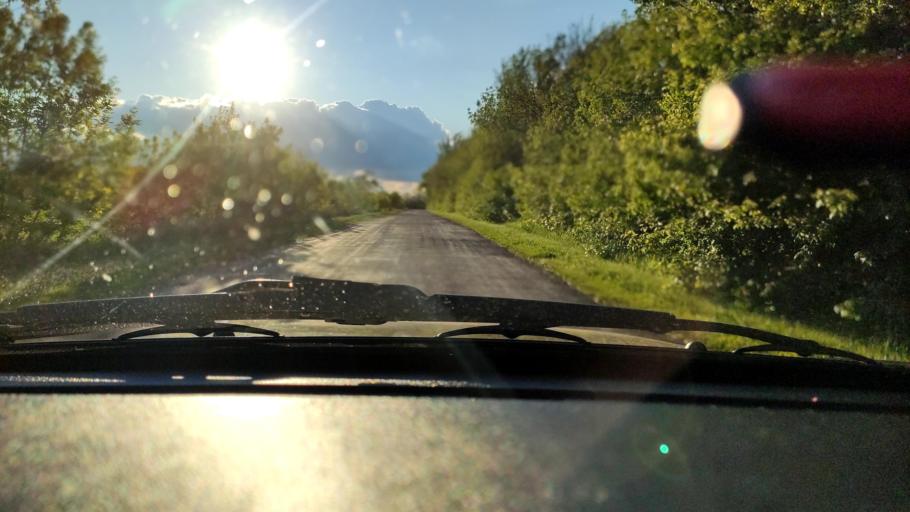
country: RU
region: Voronezj
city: Uryv-Pokrovka
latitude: 51.1453
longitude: 39.0647
